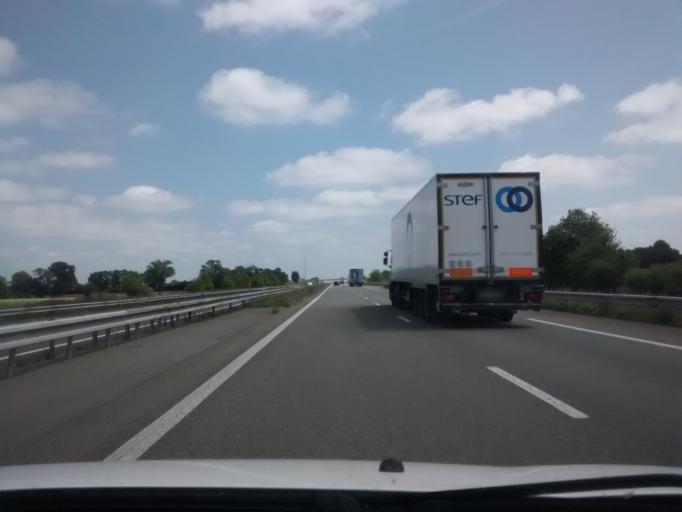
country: FR
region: Pays de la Loire
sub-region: Departement de la Mayenne
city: Soulge-sur-Ouette
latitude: 48.0709
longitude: -0.5692
